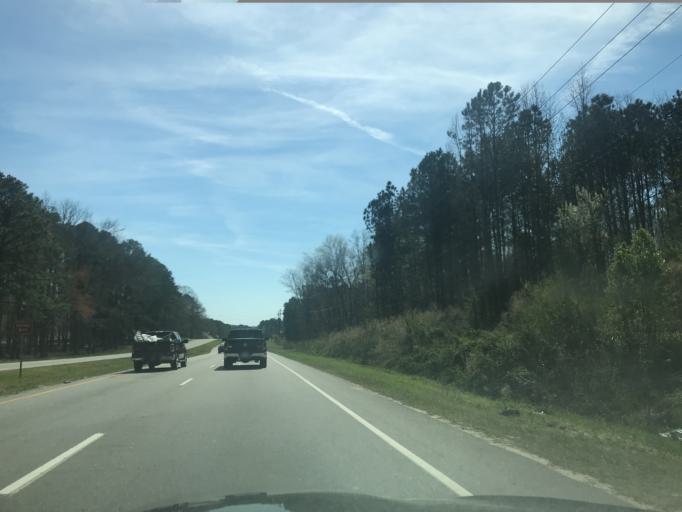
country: US
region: North Carolina
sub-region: Wake County
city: Garner
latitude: 35.6535
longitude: -78.7063
